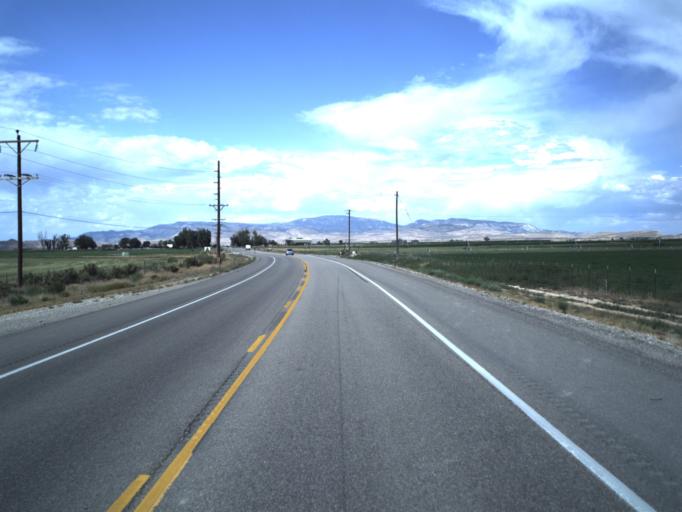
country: US
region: Utah
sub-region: Sanpete County
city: Centerfield
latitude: 39.0824
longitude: -111.8204
